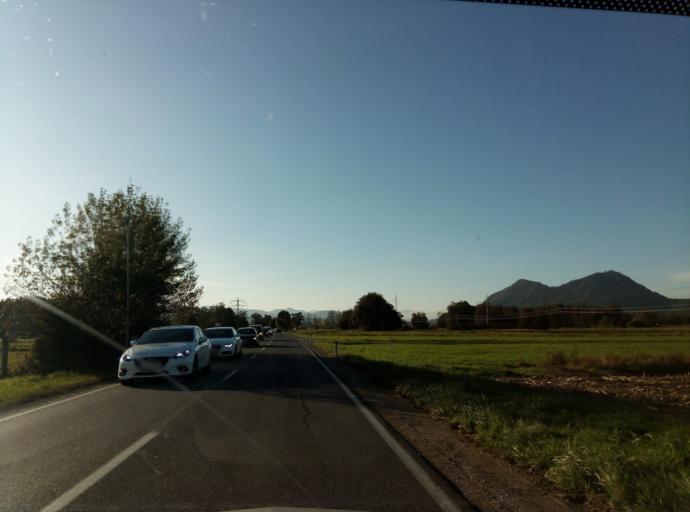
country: SI
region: Ljubljana
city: Ljubljana
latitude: 46.1032
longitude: 14.5002
